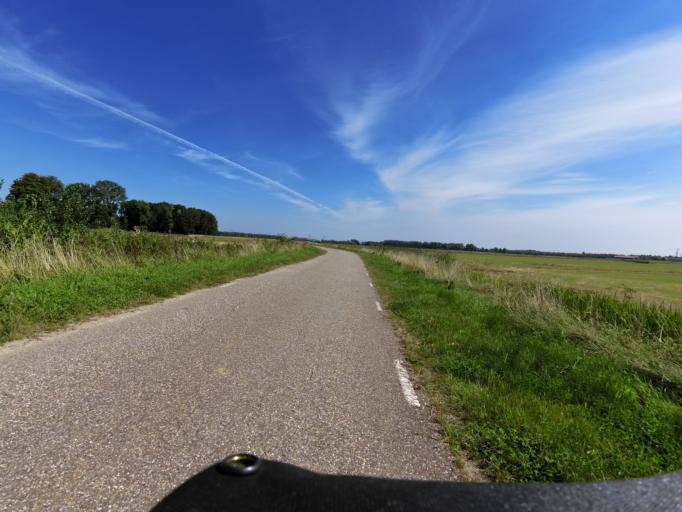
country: NL
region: South Holland
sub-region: Gemeente Sliedrecht
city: Sliedrecht
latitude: 51.7725
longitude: 4.8174
